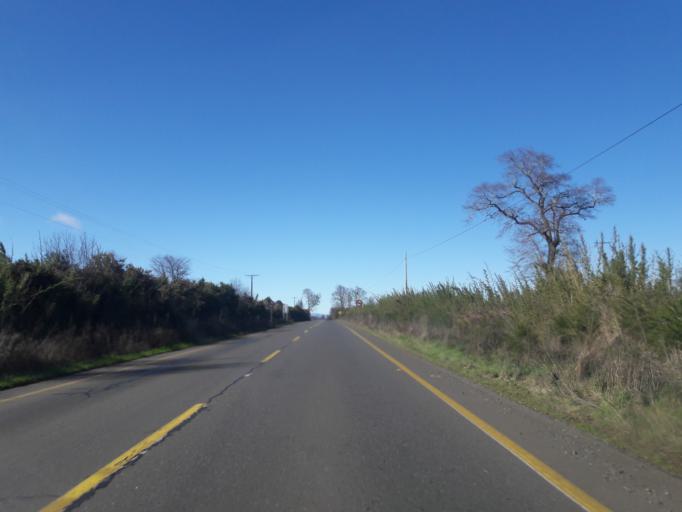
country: CL
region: Araucania
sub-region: Provincia de Malleco
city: Victoria
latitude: -38.2607
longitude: -72.2509
